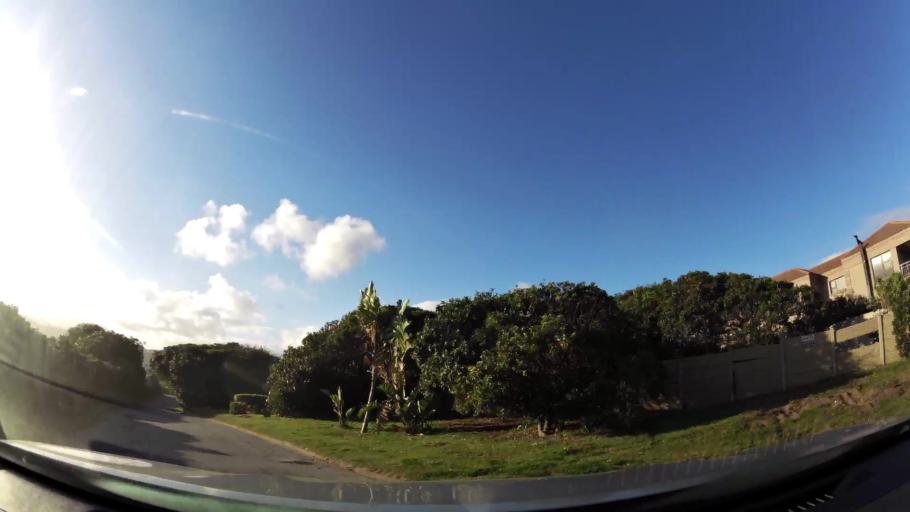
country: ZA
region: Western Cape
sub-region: Eden District Municipality
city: George
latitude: -34.0015
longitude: 22.6353
